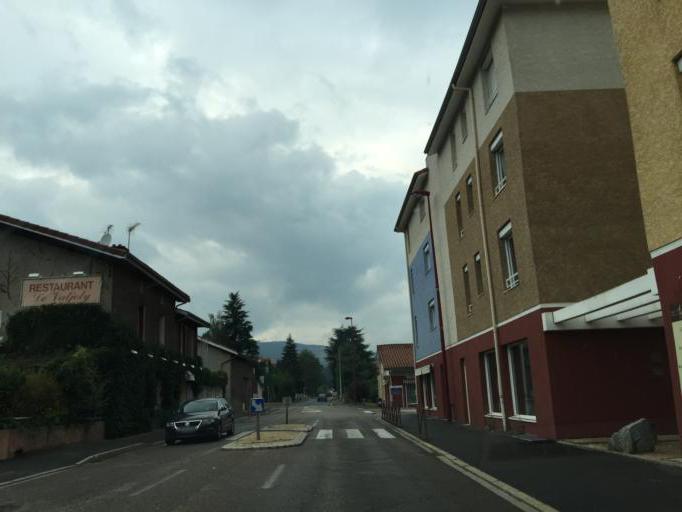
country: FR
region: Rhone-Alpes
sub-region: Departement de la Loire
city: La Talaudiere
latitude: 45.4939
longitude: 4.4353
